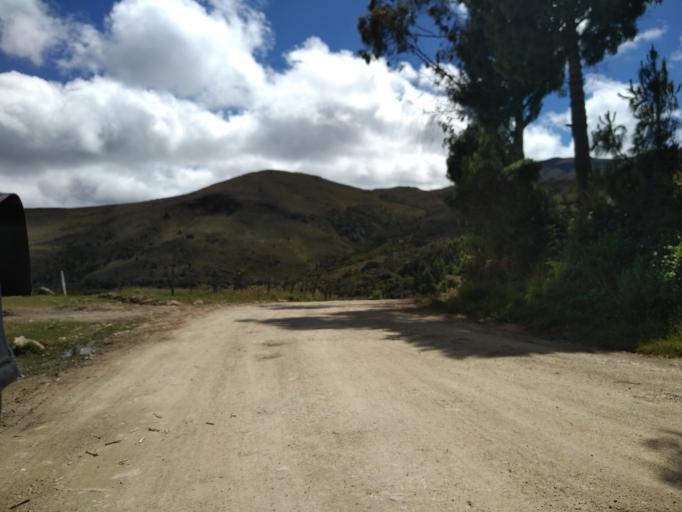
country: CO
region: Boyaca
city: Duitama
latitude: 5.9296
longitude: -73.0888
